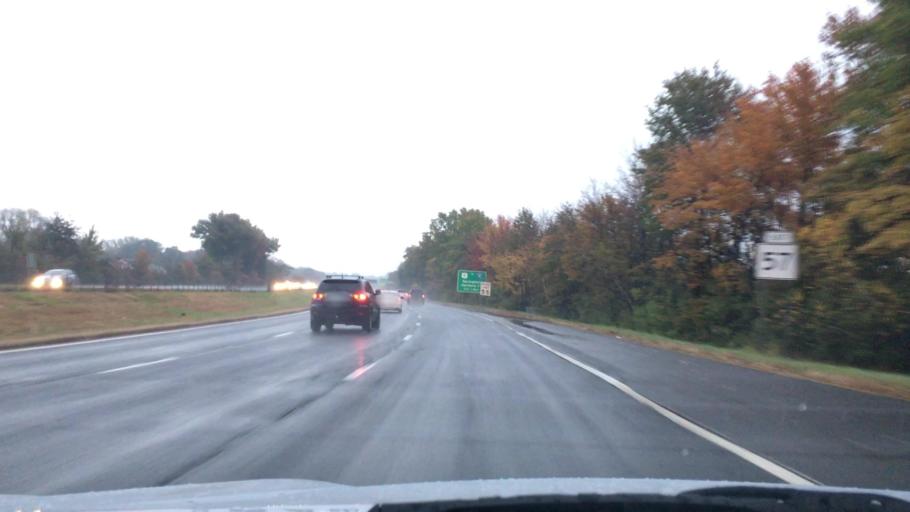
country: US
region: Massachusetts
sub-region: Hampden County
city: Agawam
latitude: 42.0755
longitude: -72.6097
